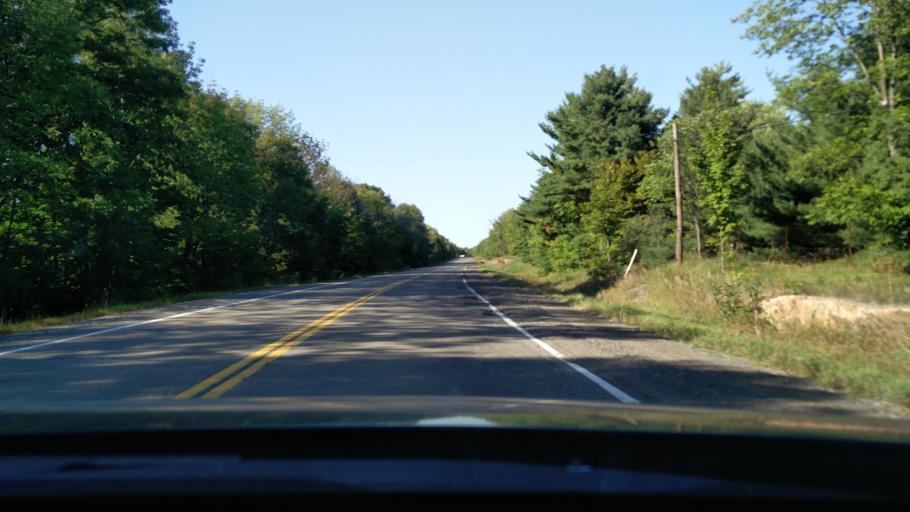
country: CA
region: Ontario
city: Perth
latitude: 44.7091
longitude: -76.4010
